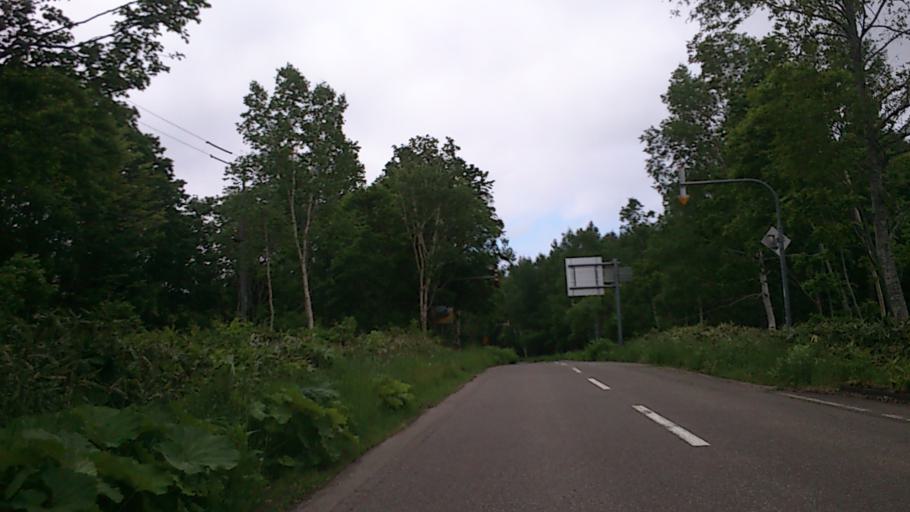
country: JP
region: Hokkaido
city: Iwanai
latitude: 42.8547
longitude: 140.5518
